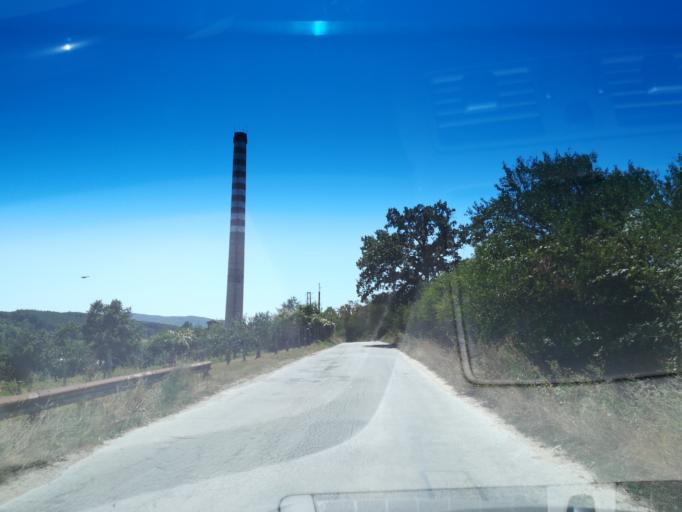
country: BG
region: Pazardzhik
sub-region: Obshtina Strelcha
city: Strelcha
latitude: 42.5220
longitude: 24.3216
